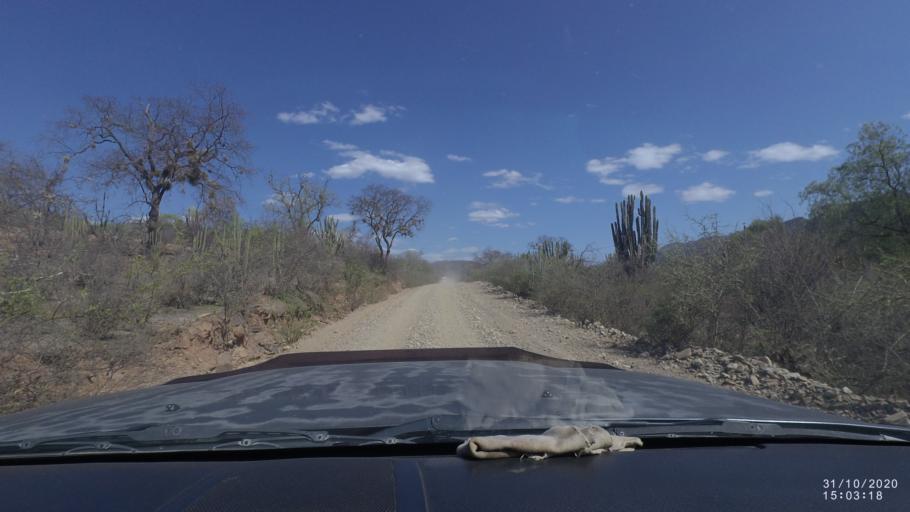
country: BO
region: Cochabamba
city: Aiquile
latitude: -18.2748
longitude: -64.8074
